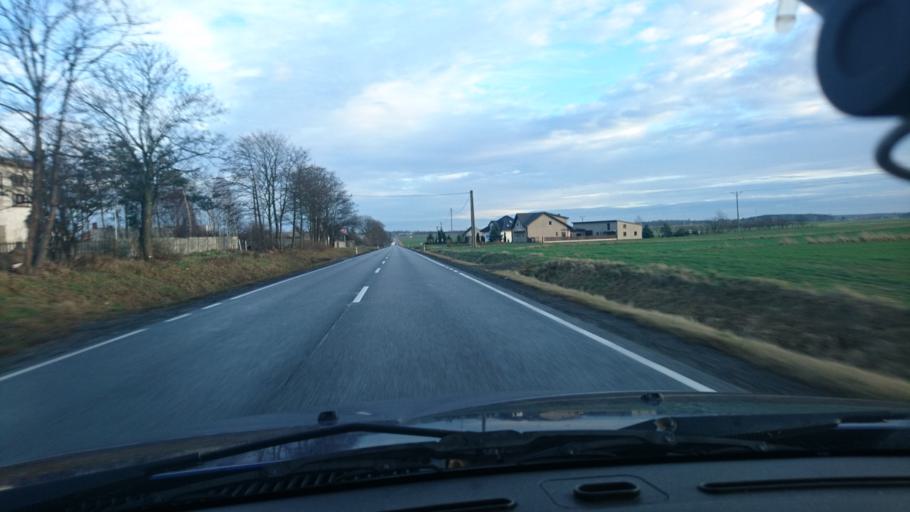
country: PL
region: Greater Poland Voivodeship
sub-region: Powiat kepinski
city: Slupia pod Kepnem
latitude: 51.2373
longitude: 18.0469
